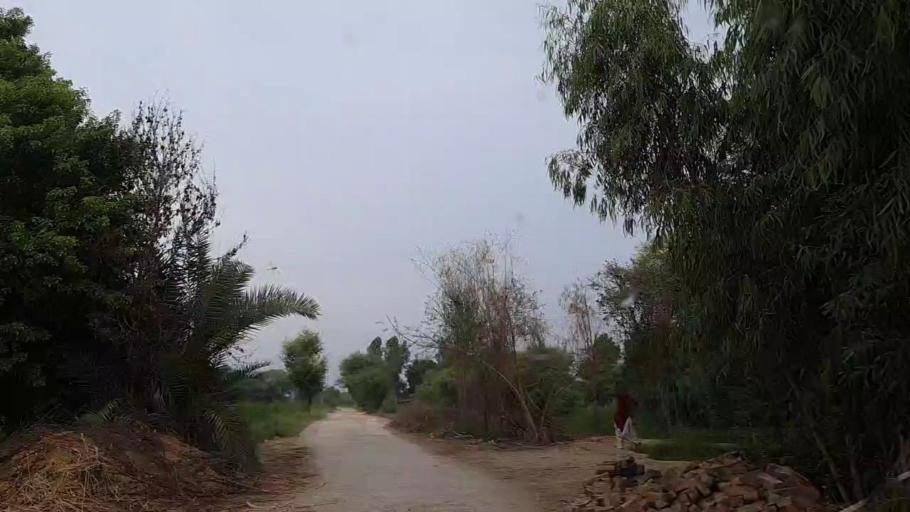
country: PK
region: Sindh
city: Khanpur
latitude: 27.8281
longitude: 69.6102
